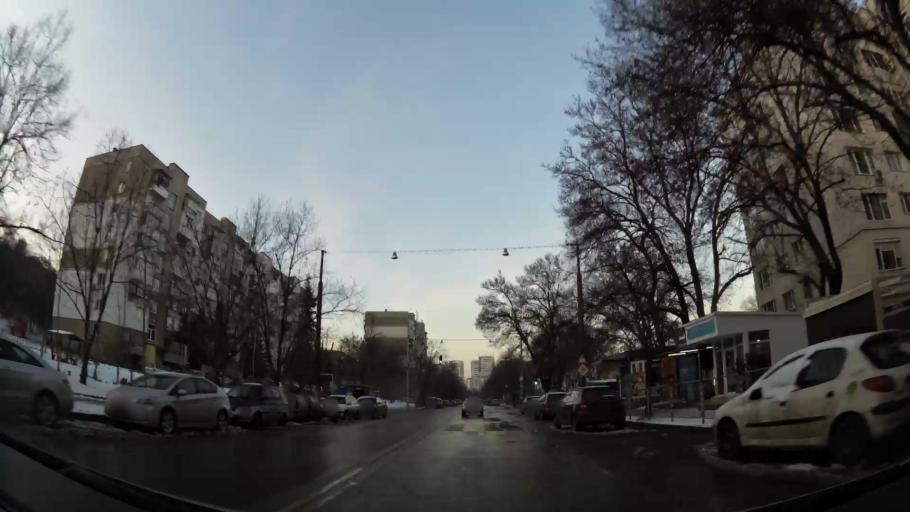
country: BG
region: Sofia-Capital
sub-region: Stolichna Obshtina
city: Sofia
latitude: 42.6843
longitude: 23.3720
